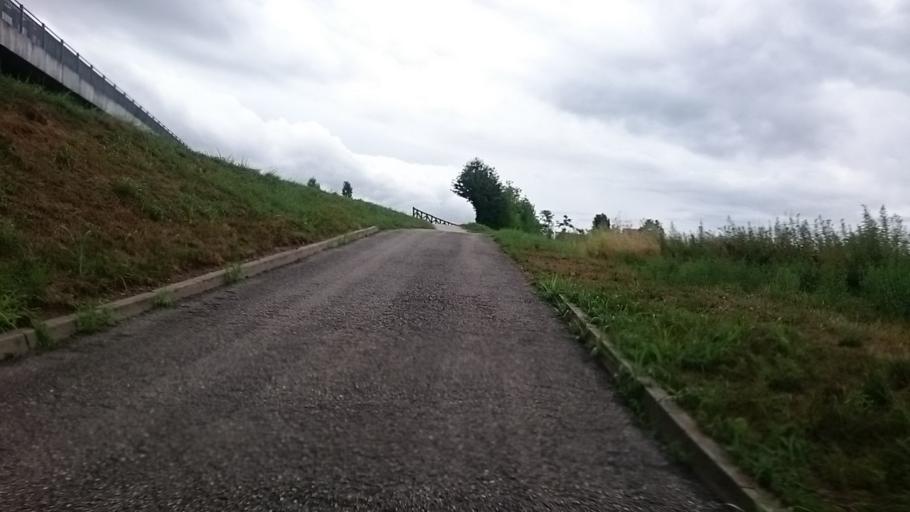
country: IT
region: Veneto
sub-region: Provincia di Treviso
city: Castelfranco Veneto
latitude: 45.6569
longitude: 11.9226
